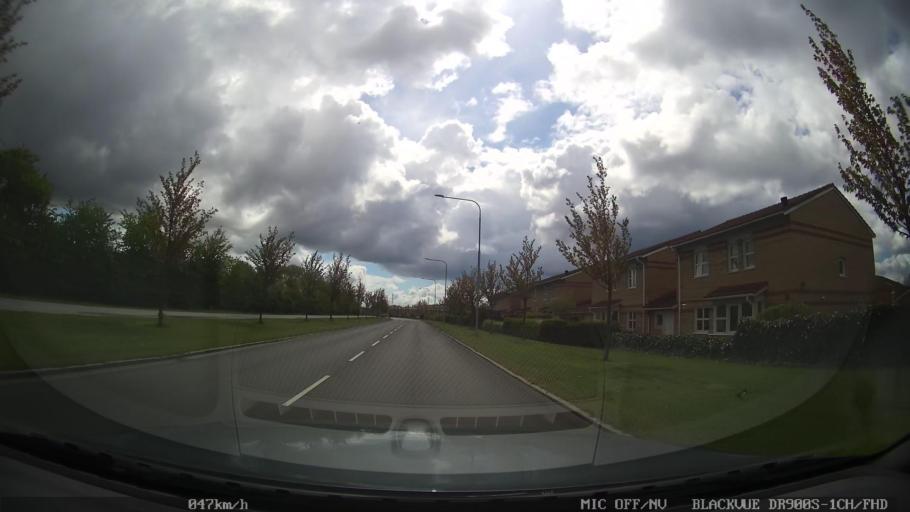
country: SE
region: Skane
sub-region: Landskrona
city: Landskrona
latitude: 55.8920
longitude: 12.8160
